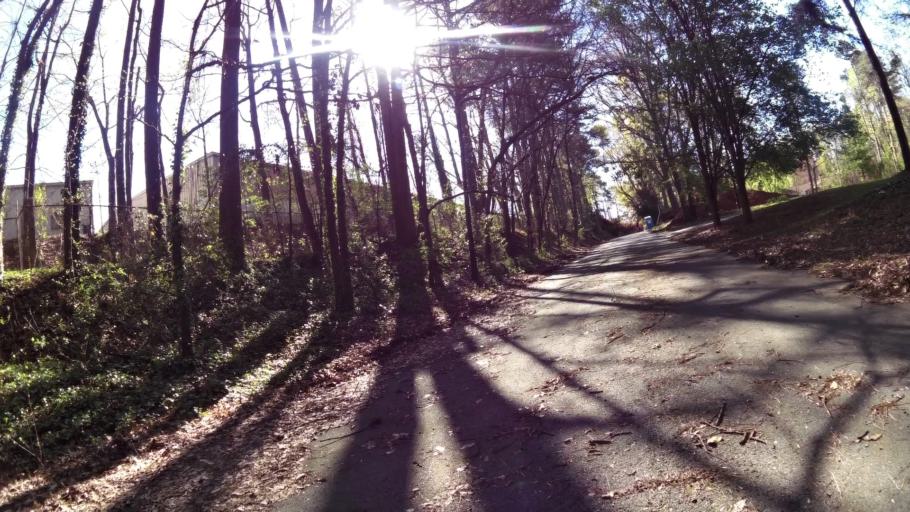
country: US
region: Georgia
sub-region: DeKalb County
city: Clarkston
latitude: 33.8309
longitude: -84.2625
